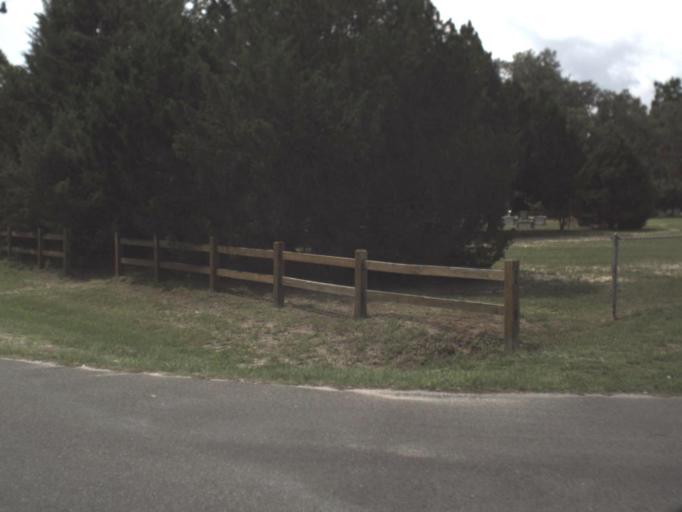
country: US
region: Florida
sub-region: Clay County
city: Keystone Heights
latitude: 29.7957
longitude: -82.0476
